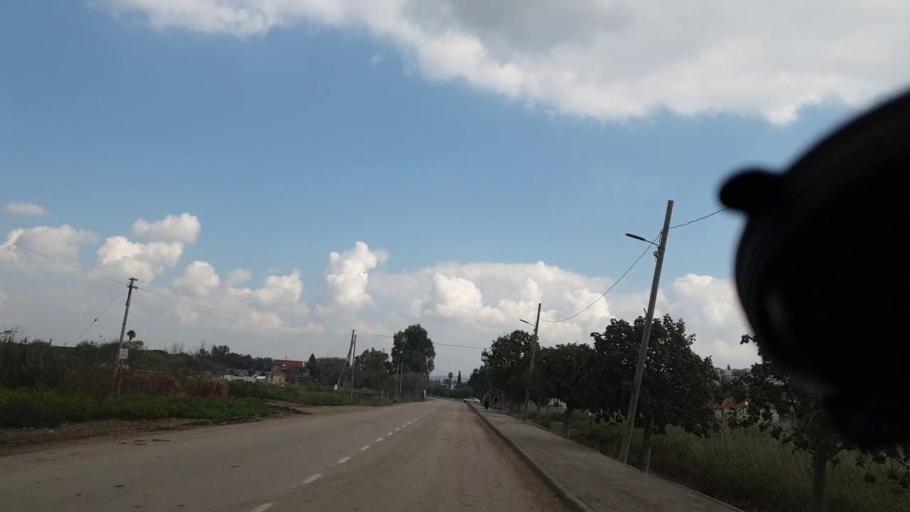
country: IL
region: Haifa
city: Rekhasim
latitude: 32.7551
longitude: 35.0871
